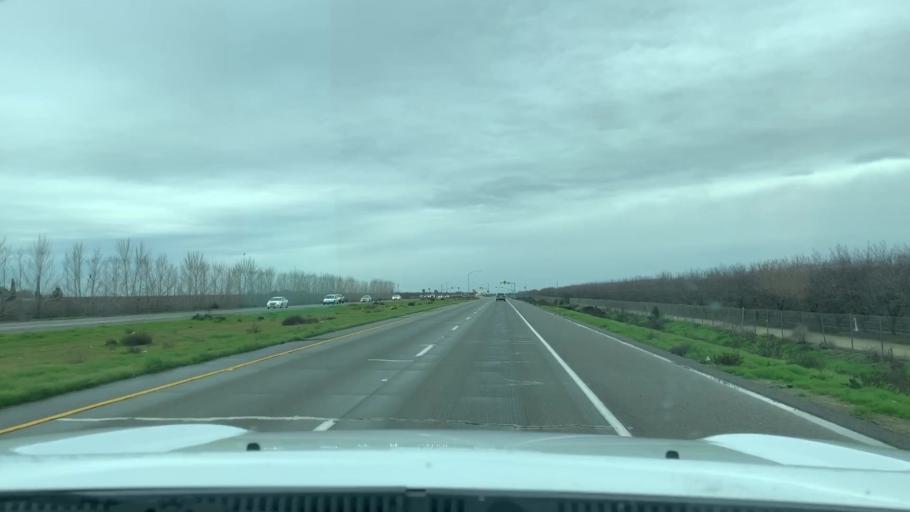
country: US
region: California
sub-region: Fresno County
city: Caruthers
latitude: 36.5132
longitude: -119.7860
